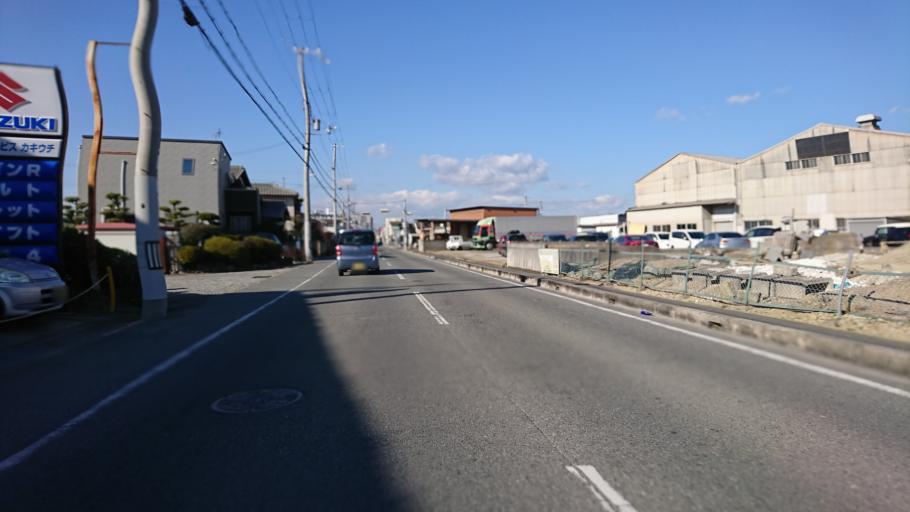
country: JP
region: Hyogo
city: Kakogawacho-honmachi
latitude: 34.7353
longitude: 134.8653
